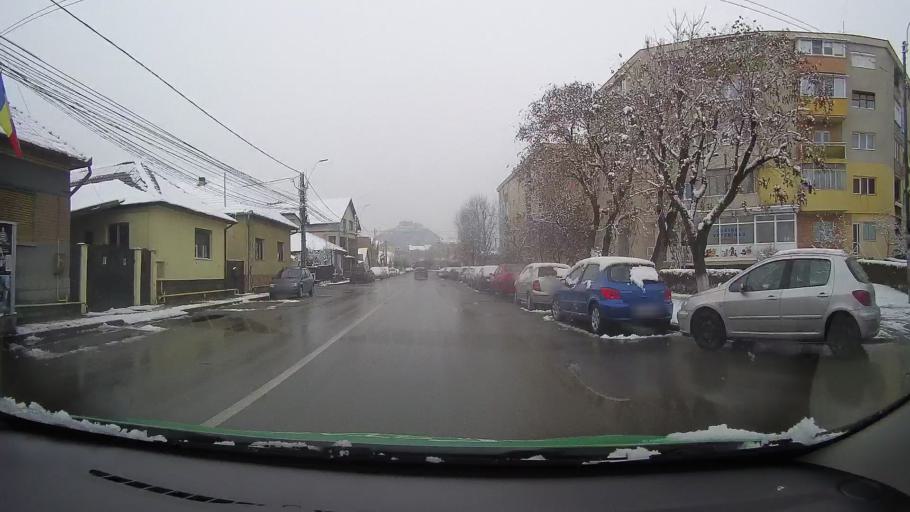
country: RO
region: Hunedoara
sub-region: Municipiul Deva
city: Deva
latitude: 45.8717
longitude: 22.9027
